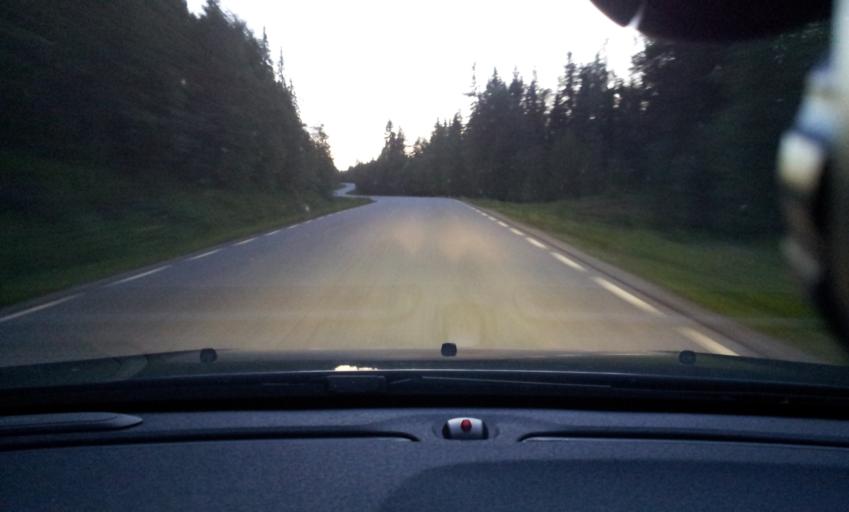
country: SE
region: Jaemtland
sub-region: Braecke Kommun
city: Braecke
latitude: 62.7286
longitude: 15.4070
